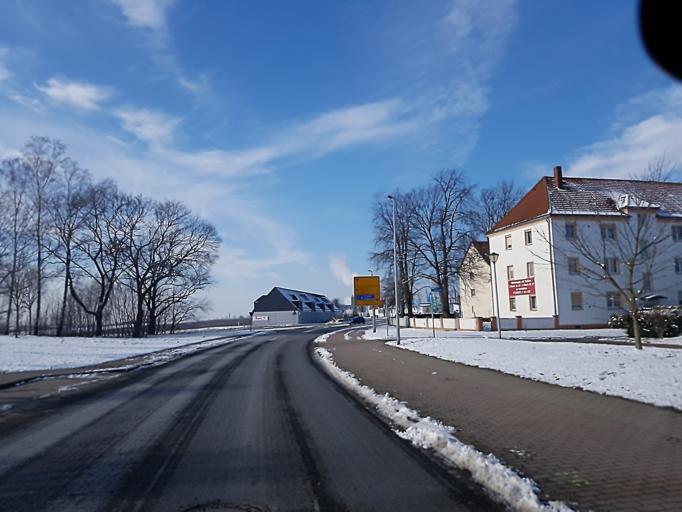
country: DE
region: Saxony
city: Leisnig
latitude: 51.1552
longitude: 12.9169
